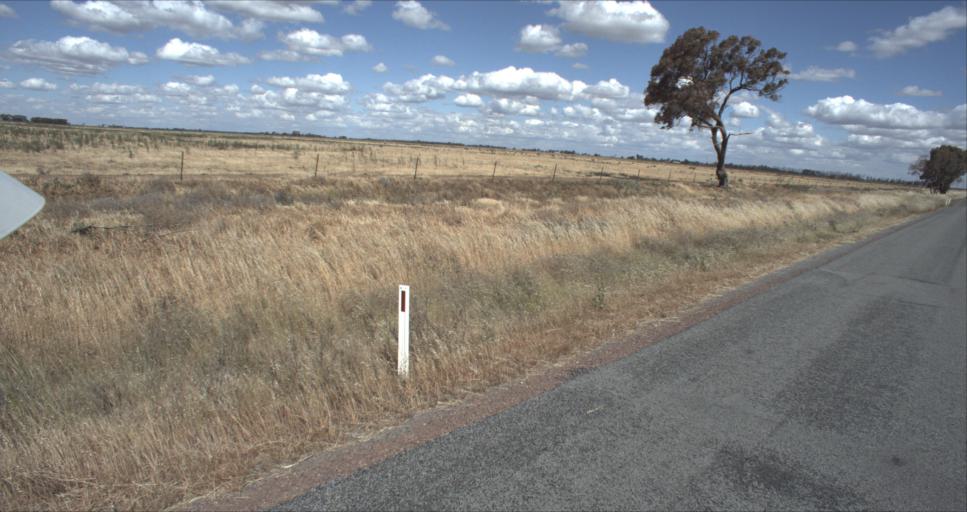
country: AU
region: New South Wales
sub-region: Leeton
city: Leeton
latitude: -34.4926
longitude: 146.2470
